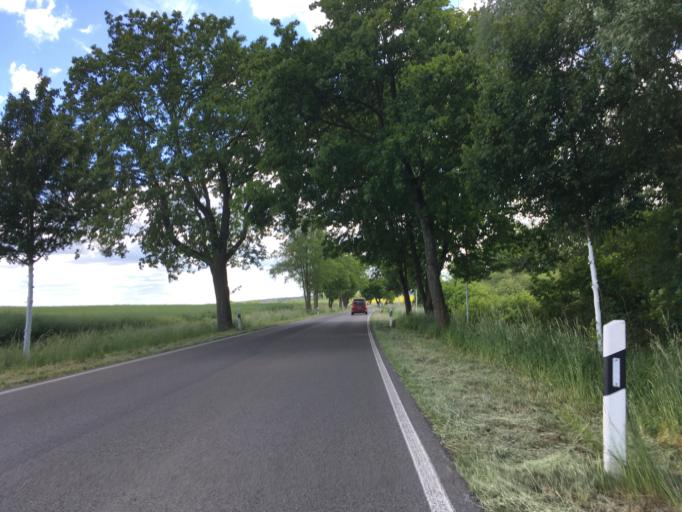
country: DE
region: Brandenburg
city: Protzel
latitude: 52.6577
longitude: 13.9895
